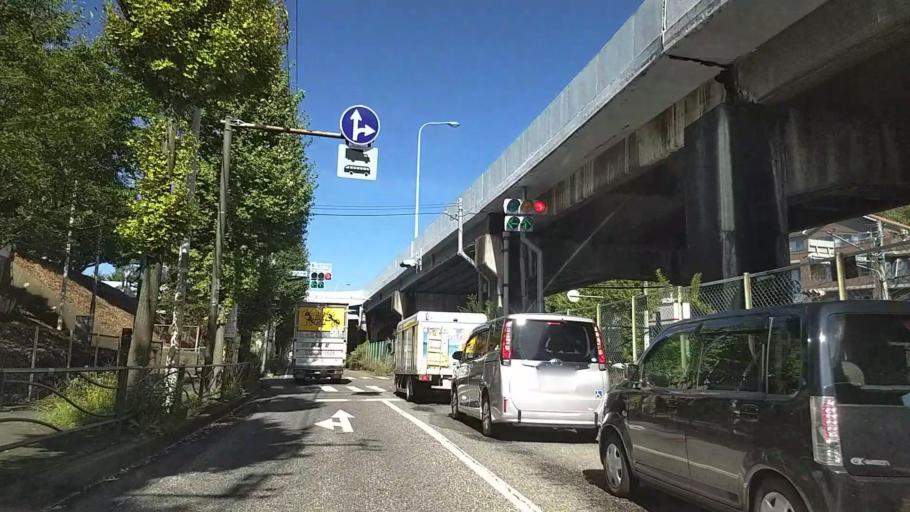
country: JP
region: Tokyo
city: Chofugaoka
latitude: 35.5813
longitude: 139.6088
